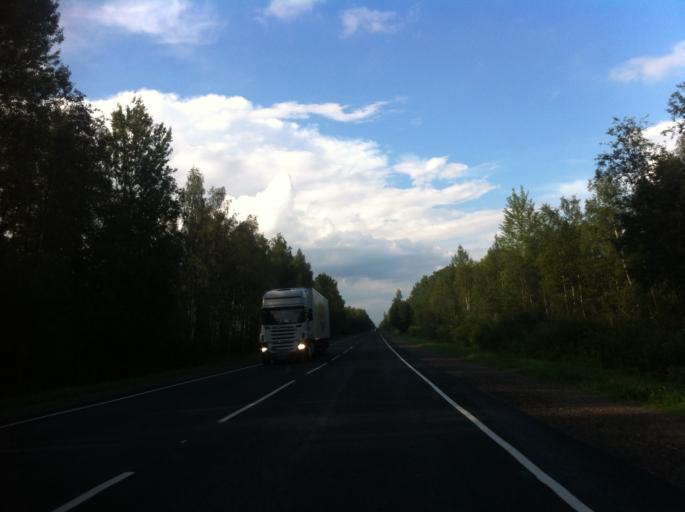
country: RU
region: Leningrad
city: Luga
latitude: 58.4675
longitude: 29.7678
